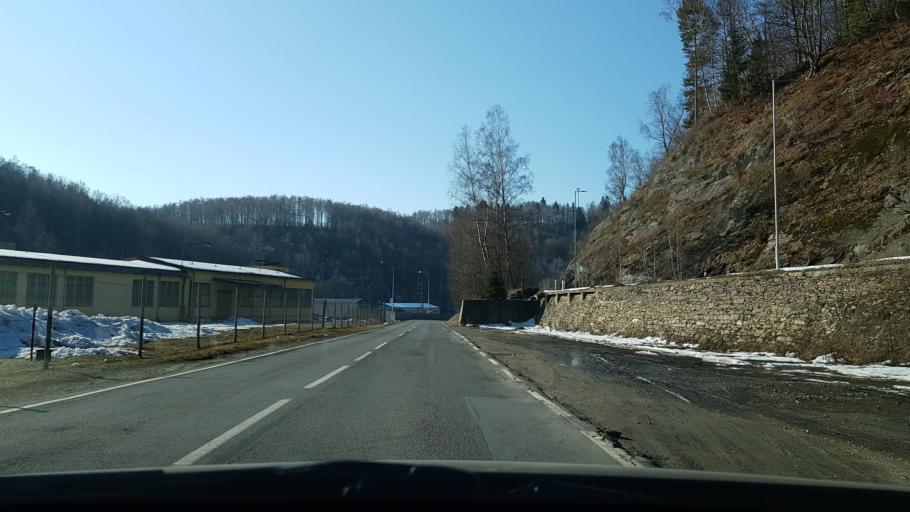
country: CZ
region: Olomoucky
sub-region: Okres Sumperk
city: Hanusovice
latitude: 50.0979
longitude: 16.9888
